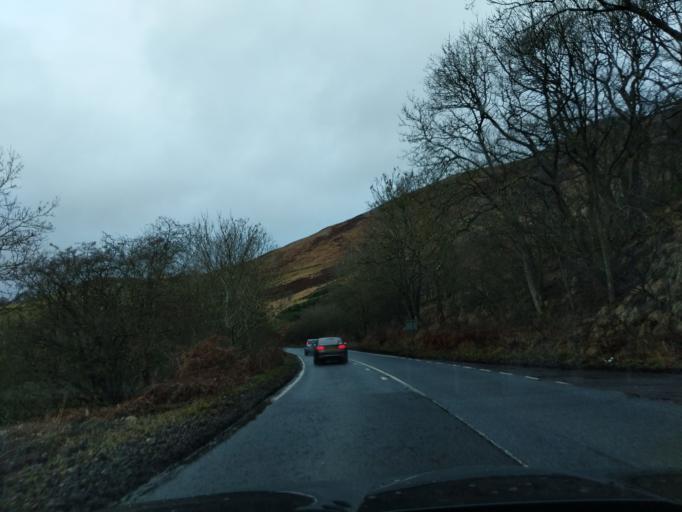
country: GB
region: Scotland
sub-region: The Scottish Borders
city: Galashiels
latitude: 55.6621
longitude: -2.8603
